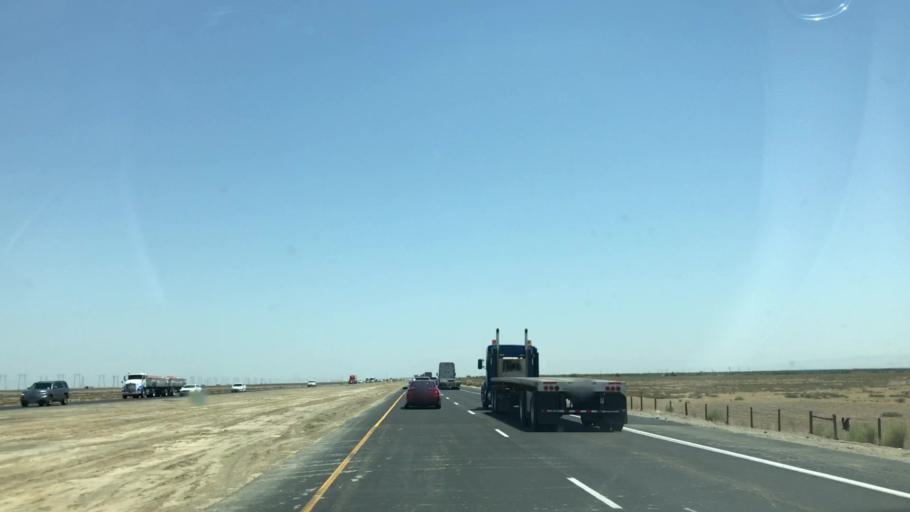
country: US
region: California
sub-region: Kern County
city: Lost Hills
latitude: 35.8155
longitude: -119.8019
